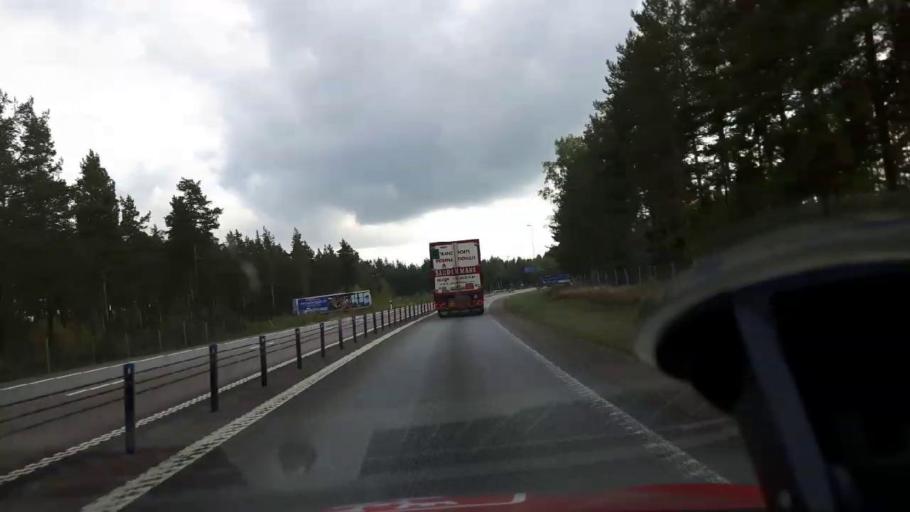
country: SE
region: Gaevleborg
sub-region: Gavle Kommun
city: Norrsundet
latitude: 60.9624
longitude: 17.0327
